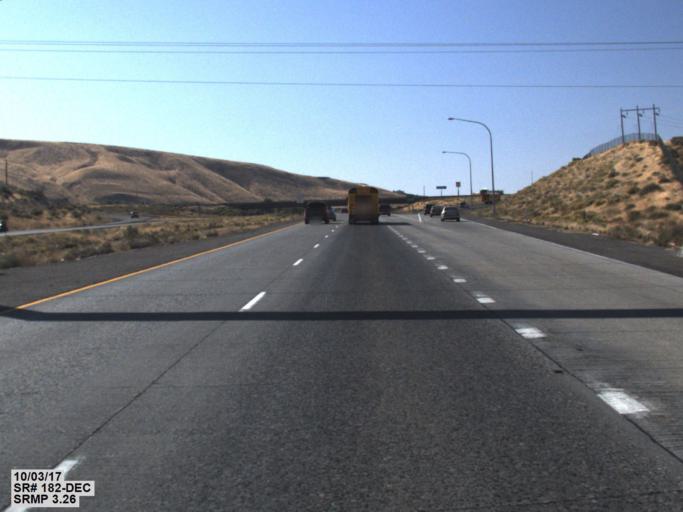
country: US
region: Washington
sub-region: Benton County
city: Richland
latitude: 46.2568
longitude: -119.2977
